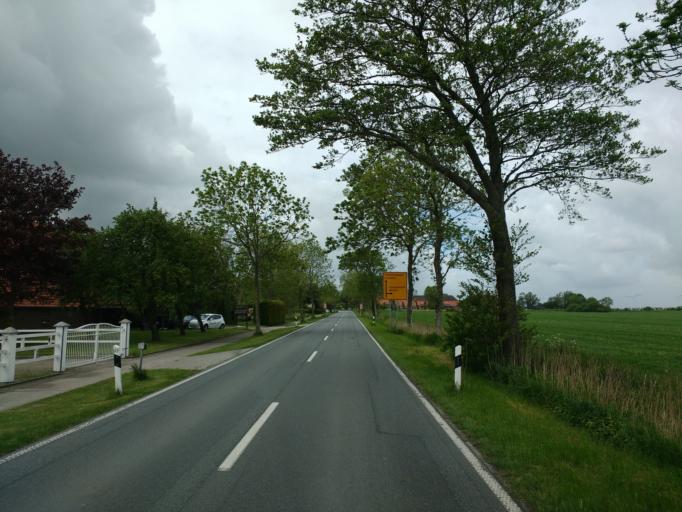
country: DE
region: Lower Saxony
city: Schillig
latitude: 53.6844
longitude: 7.9932
